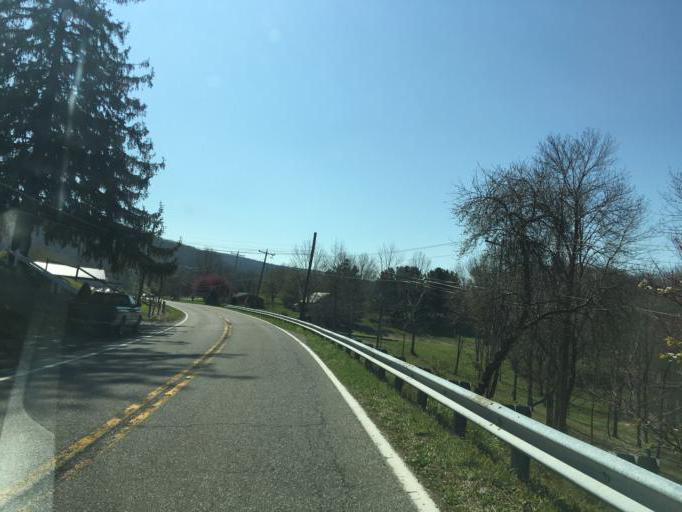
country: US
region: Maryland
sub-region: Frederick County
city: Myersville
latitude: 39.5659
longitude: -77.5303
